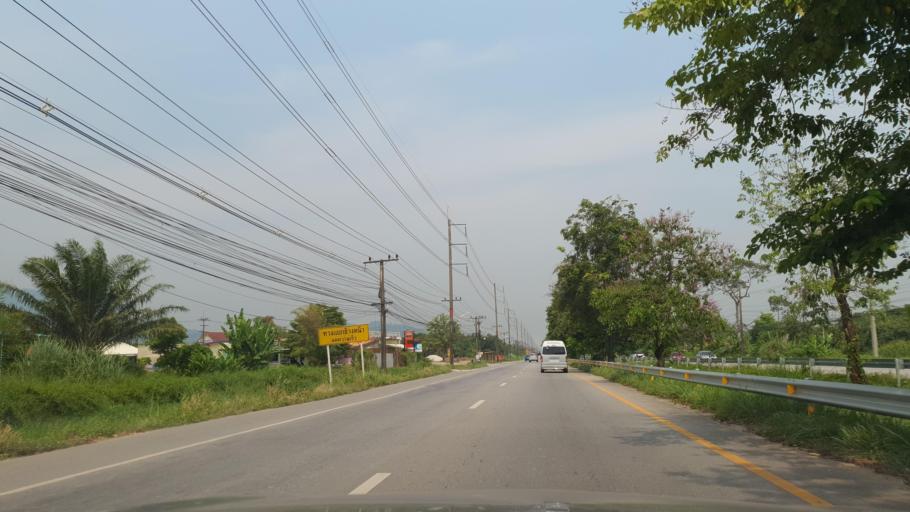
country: TH
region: Rayong
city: Rayong
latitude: 12.6391
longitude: 101.3750
